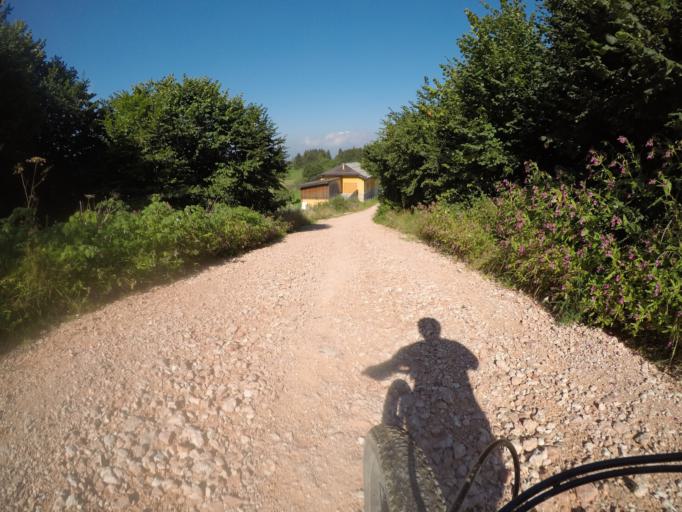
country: IT
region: Veneto
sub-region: Provincia di Vicenza
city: Canove di Roana
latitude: 45.8387
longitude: 11.5004
